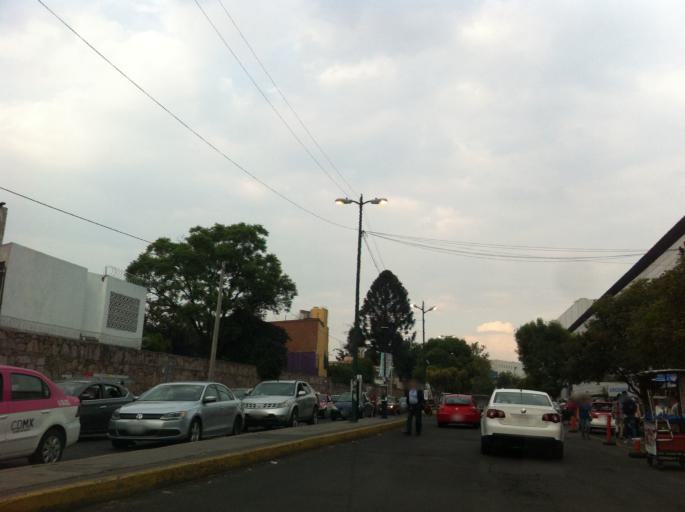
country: MX
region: Mexico
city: Colonia Lindavista
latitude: 19.4873
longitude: -99.1341
